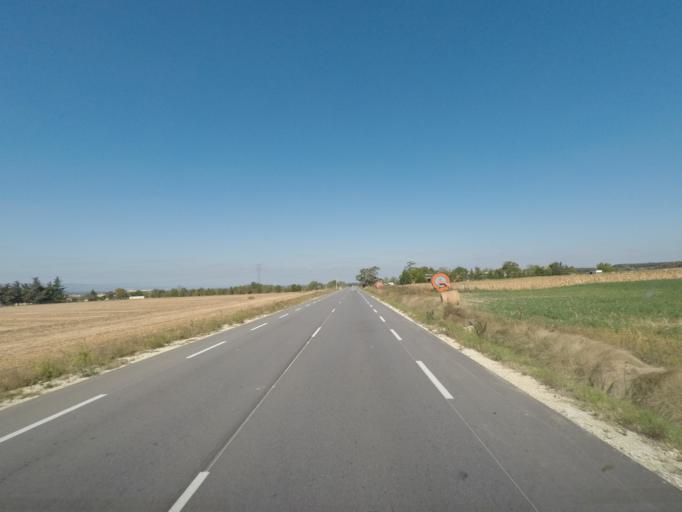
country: FR
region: Rhone-Alpes
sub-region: Departement de la Drome
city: Montmeyran
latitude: 44.8448
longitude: 5.0087
